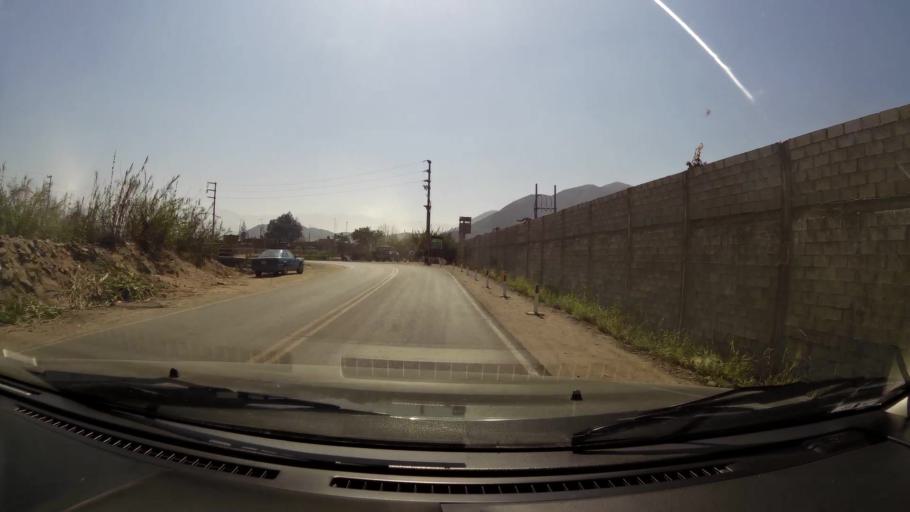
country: PE
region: Ica
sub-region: Provincia de Ica
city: San Juan Bautista
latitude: -13.9806
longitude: -75.6980
